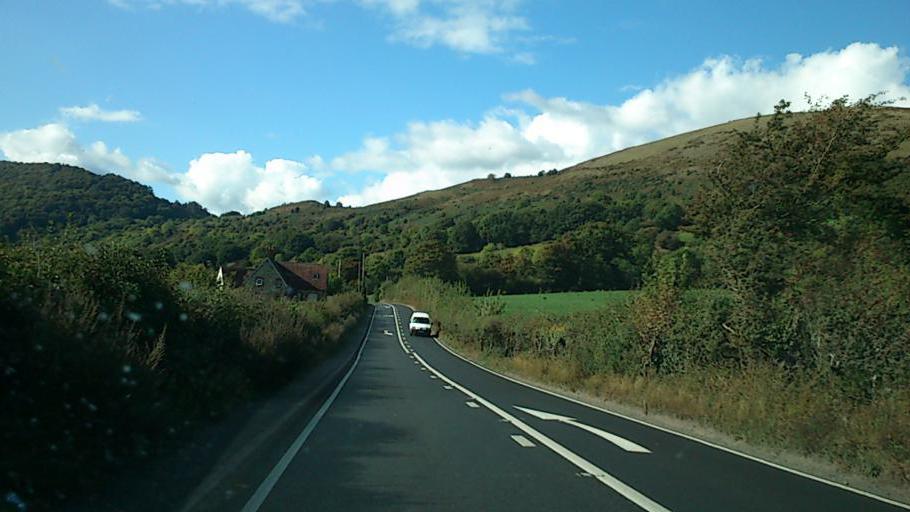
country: GB
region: England
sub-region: Shropshire
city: Westbury
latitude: 52.7078
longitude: -3.0191
